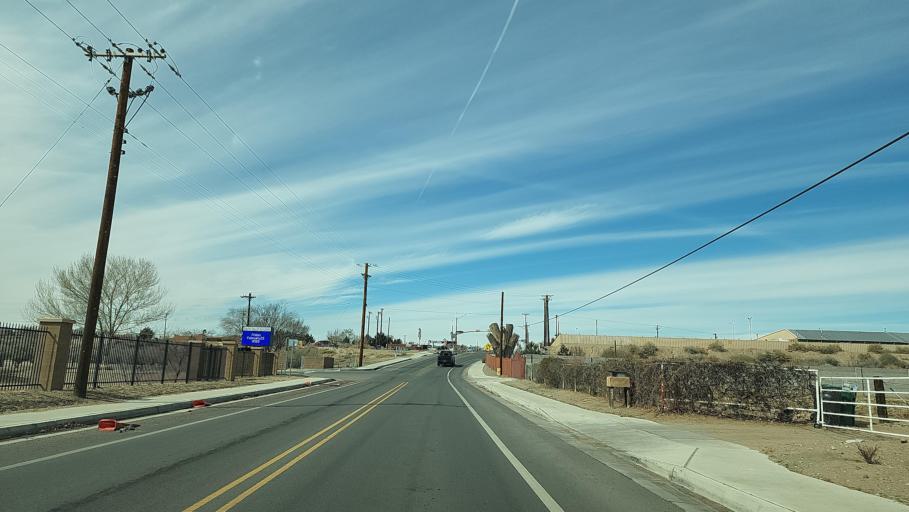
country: US
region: New Mexico
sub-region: Bernalillo County
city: South Valley
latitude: 35.0362
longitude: -106.7099
